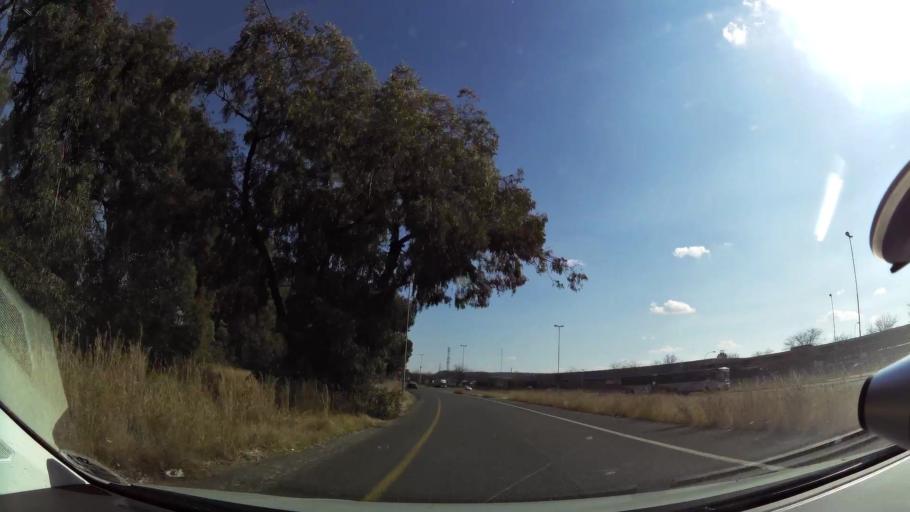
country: ZA
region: Orange Free State
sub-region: Mangaung Metropolitan Municipality
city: Bloemfontein
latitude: -29.1162
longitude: 26.2632
